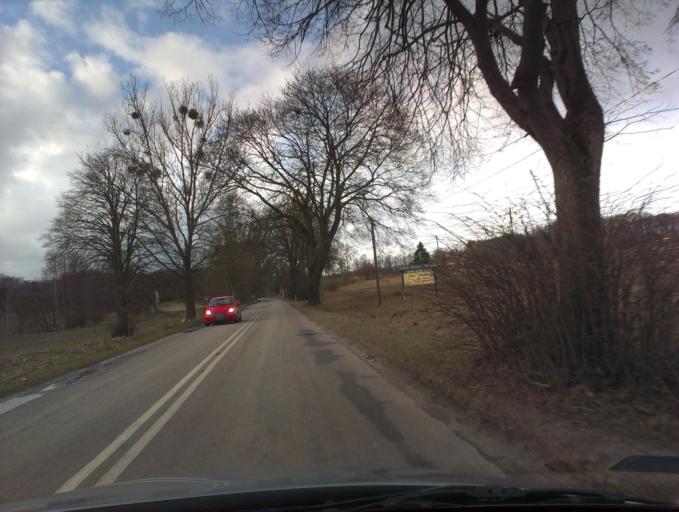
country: PL
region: Pomeranian Voivodeship
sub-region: Powiat czluchowski
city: Rzeczenica
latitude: 53.6681
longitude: 17.1087
